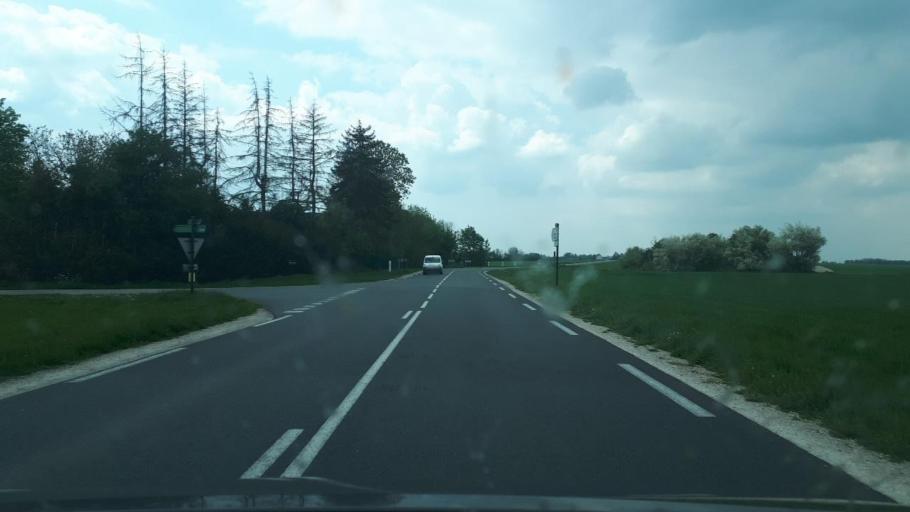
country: FR
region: Centre
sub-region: Departement du Loiret
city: Pithiviers-le-Vieil
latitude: 48.1634
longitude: 2.1313
